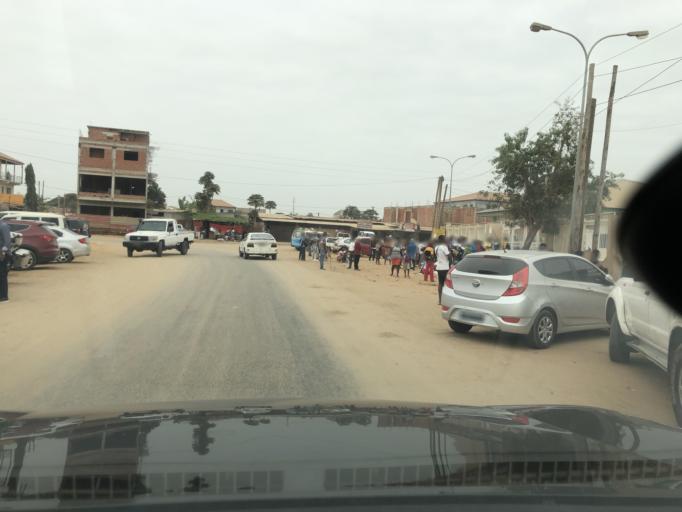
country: AO
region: Luanda
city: Luanda
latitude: -8.8992
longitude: 13.2590
